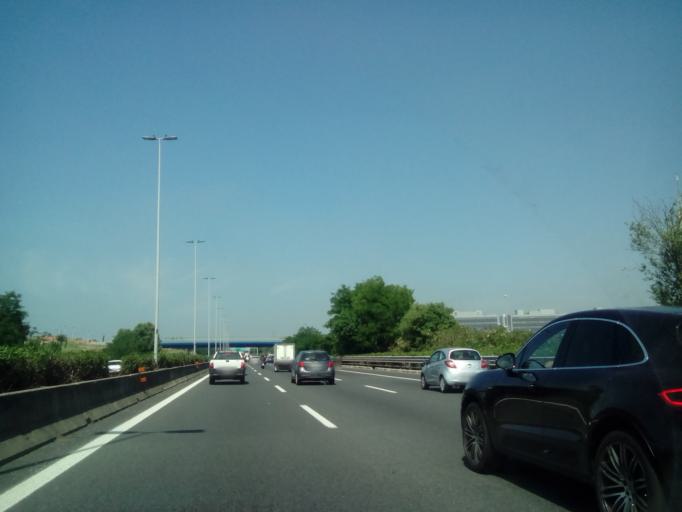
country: IT
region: Latium
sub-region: Citta metropolitana di Roma Capitale
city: Selcetta
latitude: 41.7960
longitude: 12.4943
